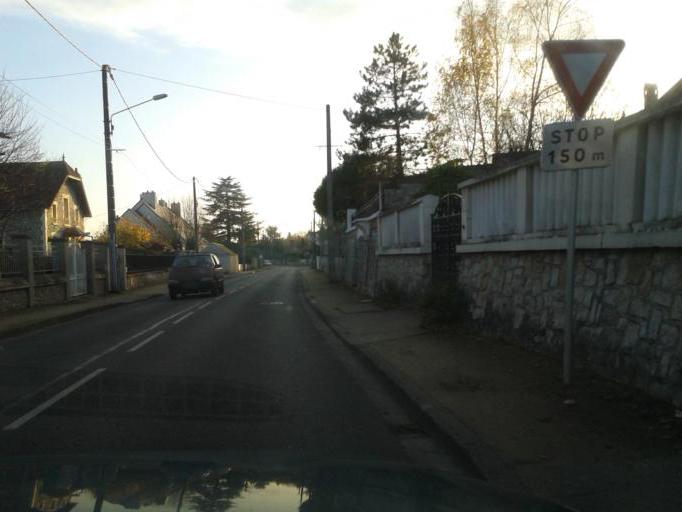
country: FR
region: Centre
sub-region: Departement du Loiret
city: Beaugency
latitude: 47.7729
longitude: 1.6298
